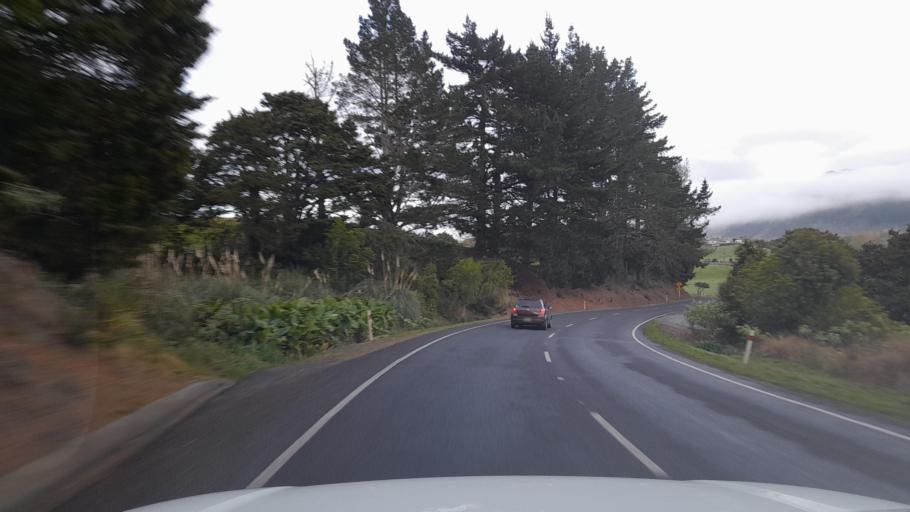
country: NZ
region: Northland
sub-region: Whangarei
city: Maungatapere
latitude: -35.7088
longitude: 173.9881
